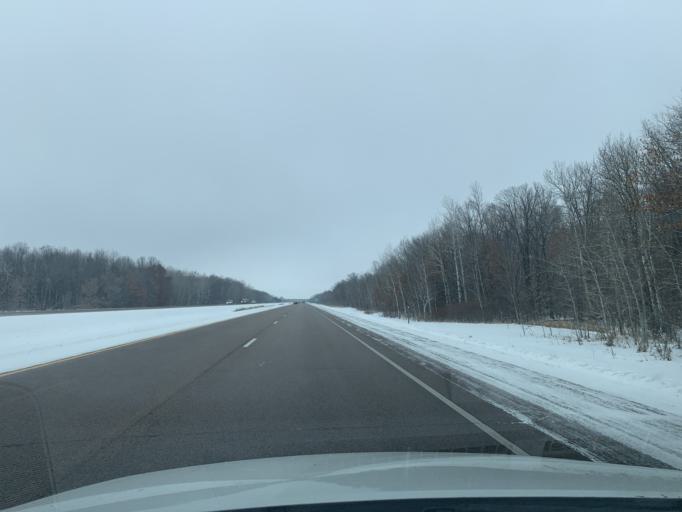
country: US
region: Minnesota
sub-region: Chisago County
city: Rush City
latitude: 45.6598
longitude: -92.9922
